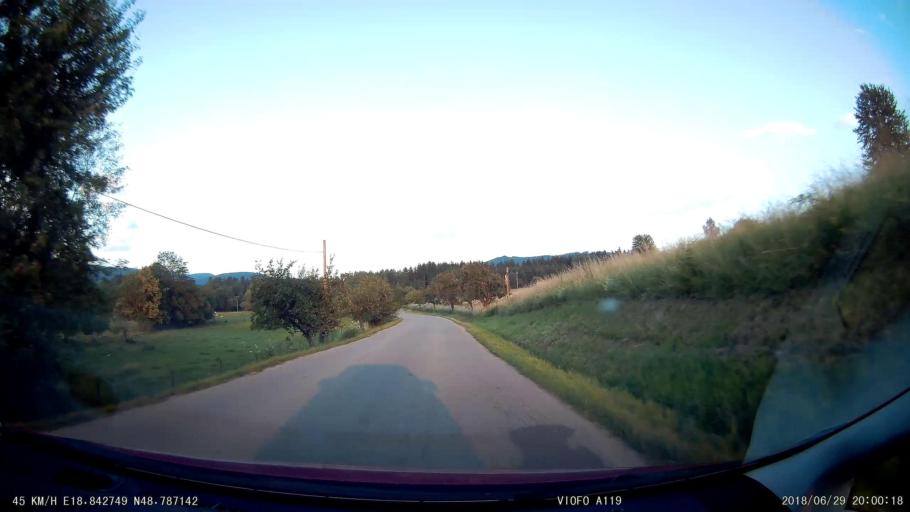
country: SK
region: Nitriansky
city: Handlova
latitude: 48.7871
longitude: 18.8429
